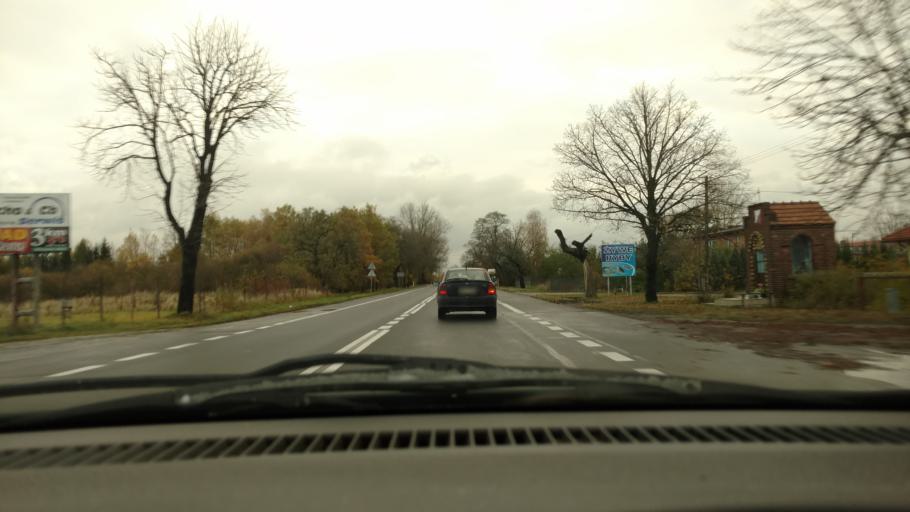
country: PL
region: Lodz Voivodeship
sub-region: Powiat laski
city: Sedziejowice
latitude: 51.5913
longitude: 19.0352
